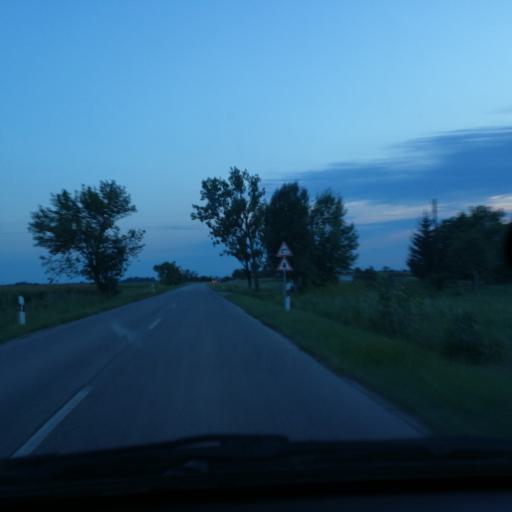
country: HU
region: Bacs-Kiskun
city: Kalocsa
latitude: 46.5106
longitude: 19.0912
